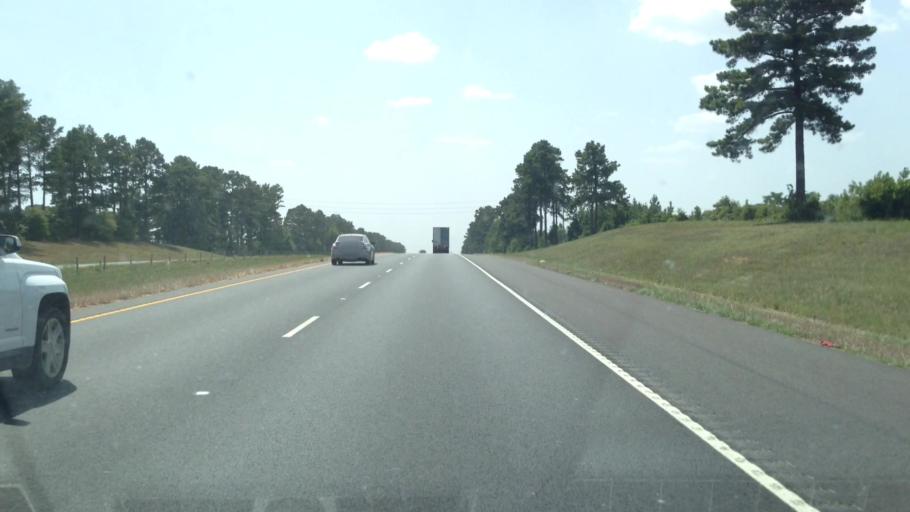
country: US
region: Louisiana
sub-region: Webster Parish
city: Minden
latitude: 32.5838
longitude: -93.2636
